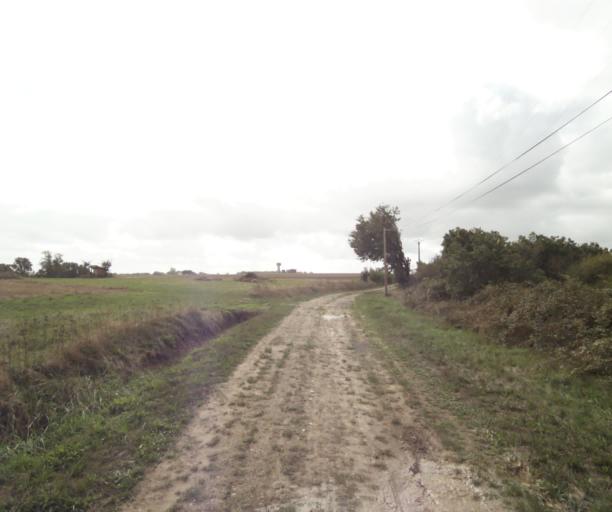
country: FR
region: Midi-Pyrenees
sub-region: Departement du Tarn-et-Garonne
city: Beaumont-de-Lomagne
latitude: 43.8828
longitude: 1.0756
